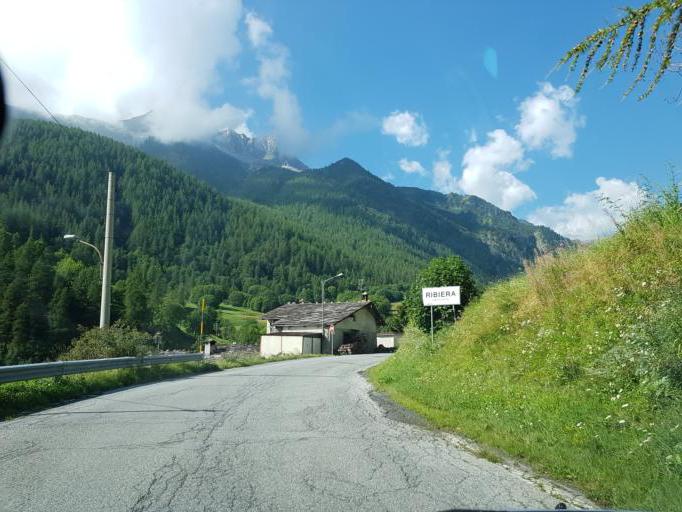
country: IT
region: Piedmont
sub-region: Provincia di Cuneo
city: Pleyne
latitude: 44.5858
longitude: 7.0396
